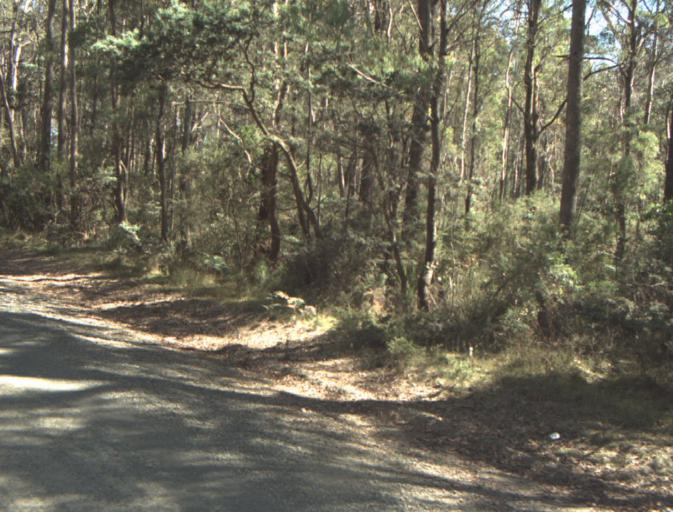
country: AU
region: Tasmania
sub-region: Launceston
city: Newstead
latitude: -41.3704
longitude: 147.2774
